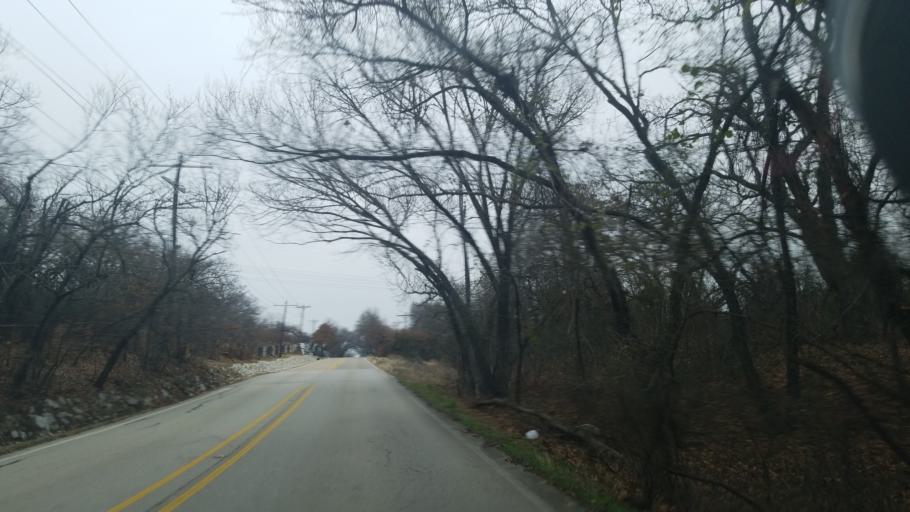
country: US
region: Texas
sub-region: Denton County
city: Copper Canyon
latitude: 33.1178
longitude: -97.1166
